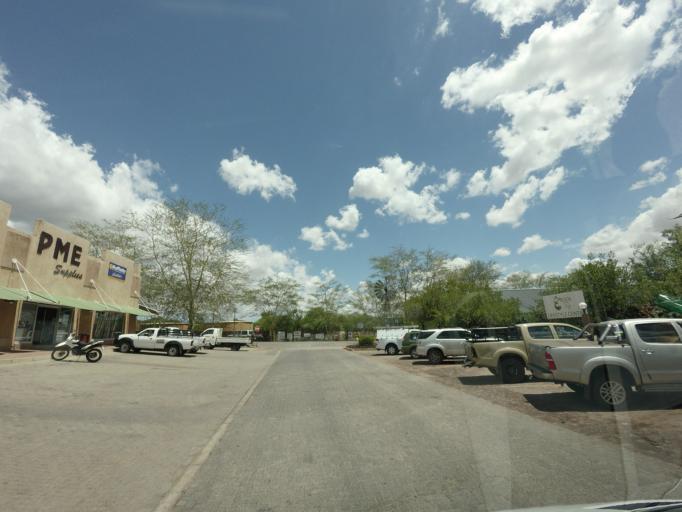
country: ZA
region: Limpopo
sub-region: Mopani District Municipality
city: Hoedspruit
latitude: -24.3505
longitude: 30.9571
